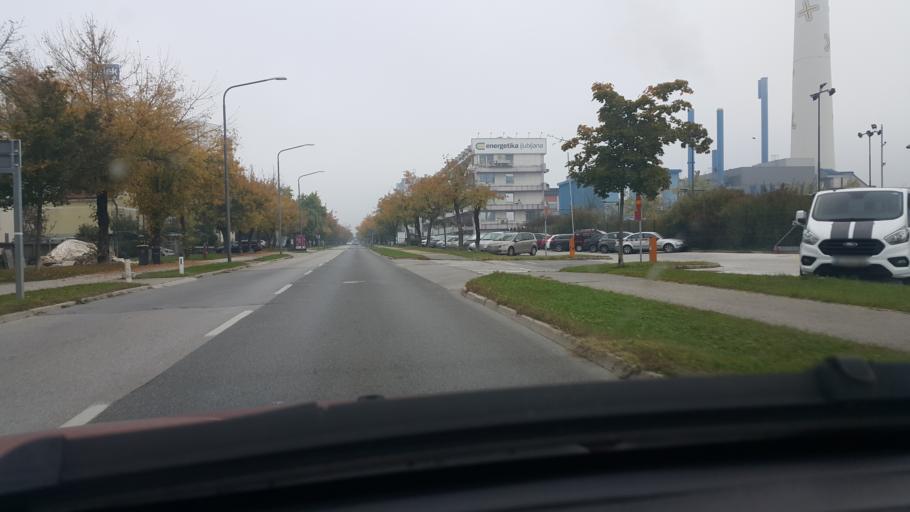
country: SI
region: Ljubljana
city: Ljubljana
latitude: 46.0749
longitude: 14.4998
